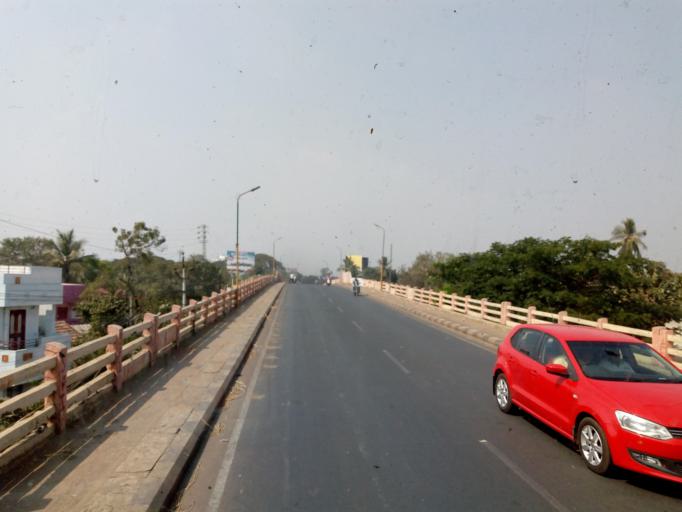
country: IN
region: Andhra Pradesh
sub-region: West Godavari
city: Eluru
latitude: 16.7088
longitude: 81.0989
